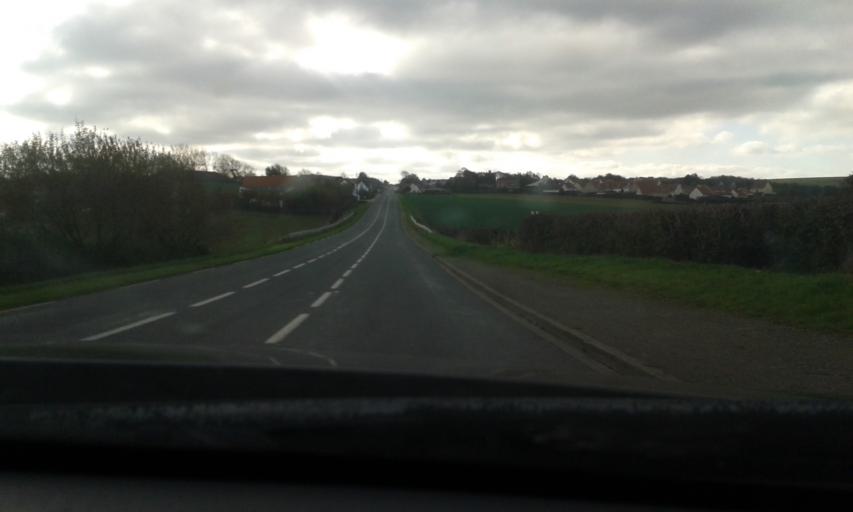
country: FR
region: Nord-Pas-de-Calais
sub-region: Departement du Pas-de-Calais
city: Ferques
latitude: 50.8740
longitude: 1.7439
